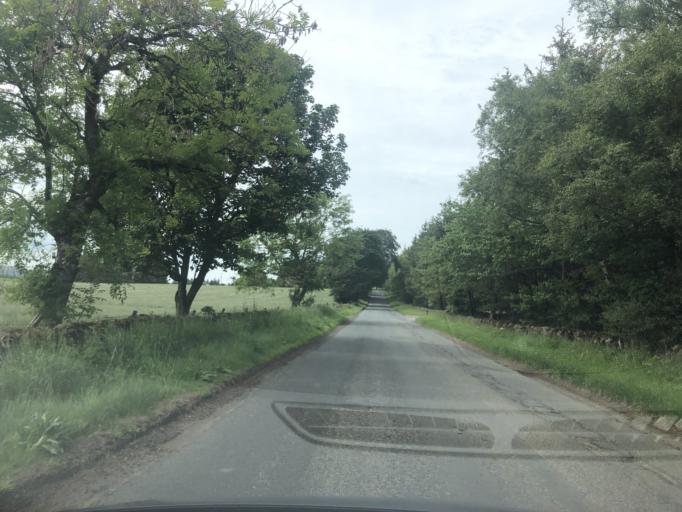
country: GB
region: Scotland
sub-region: The Scottish Borders
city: West Linton
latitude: 55.7367
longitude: -3.3326
